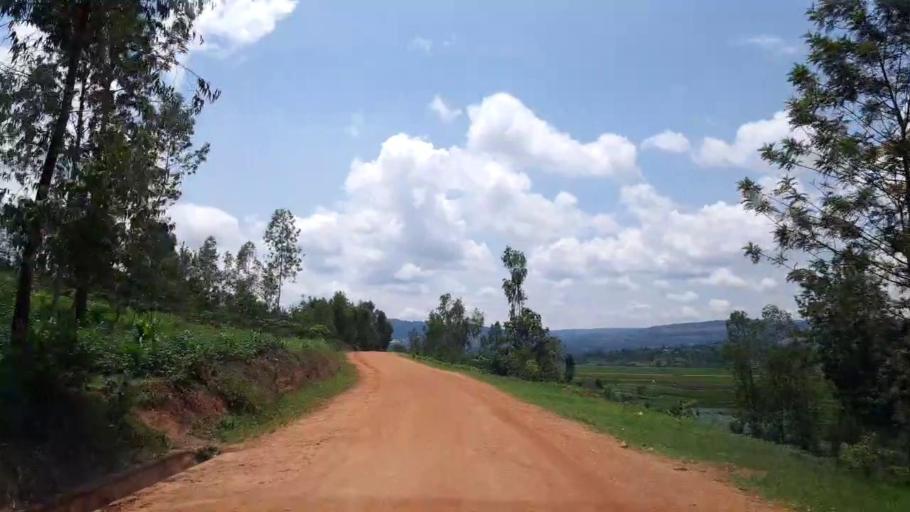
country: RW
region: Northern Province
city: Byumba
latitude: -1.5680
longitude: 30.2969
